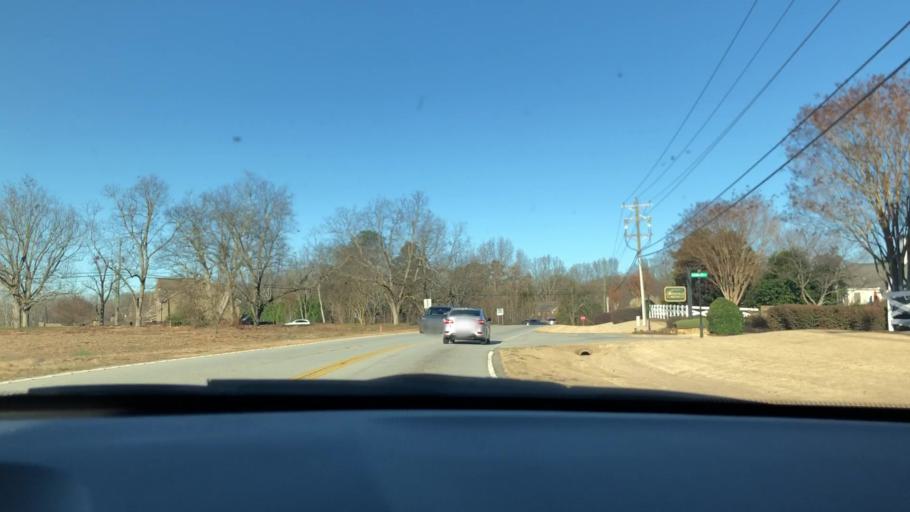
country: US
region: South Carolina
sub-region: Greenville County
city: Five Forks
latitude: 34.8322
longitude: -82.2261
